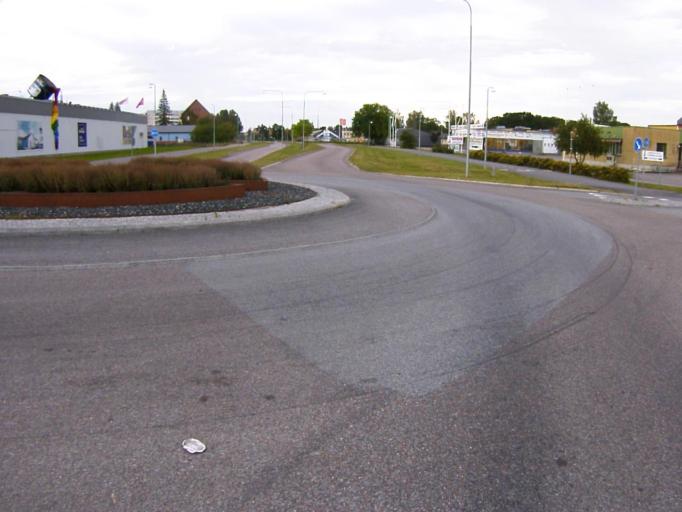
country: SE
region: Soedermanland
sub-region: Eskilstuna Kommun
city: Eskilstuna
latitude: 59.3855
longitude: 16.5054
